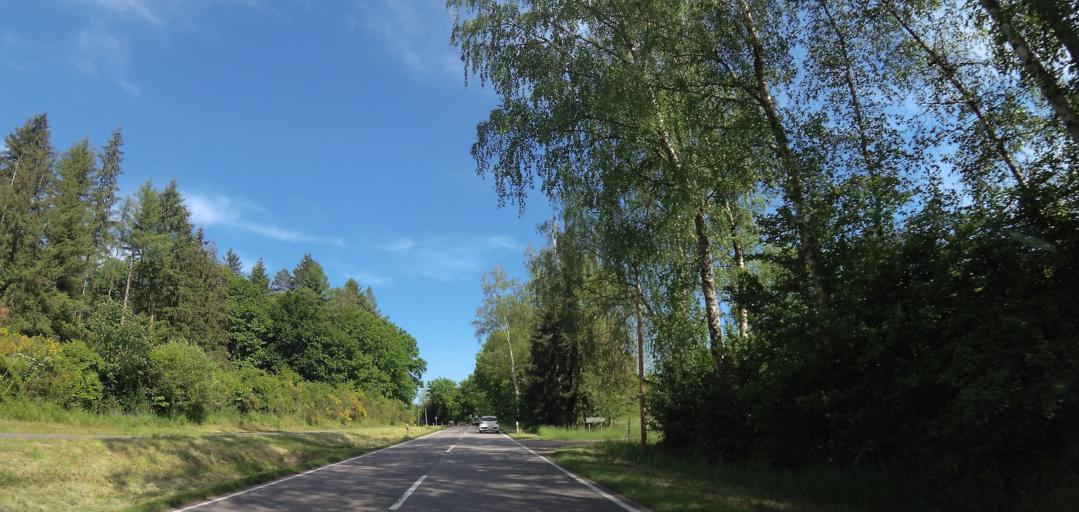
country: DE
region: Saarland
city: Losheim
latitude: 49.4509
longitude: 6.7496
